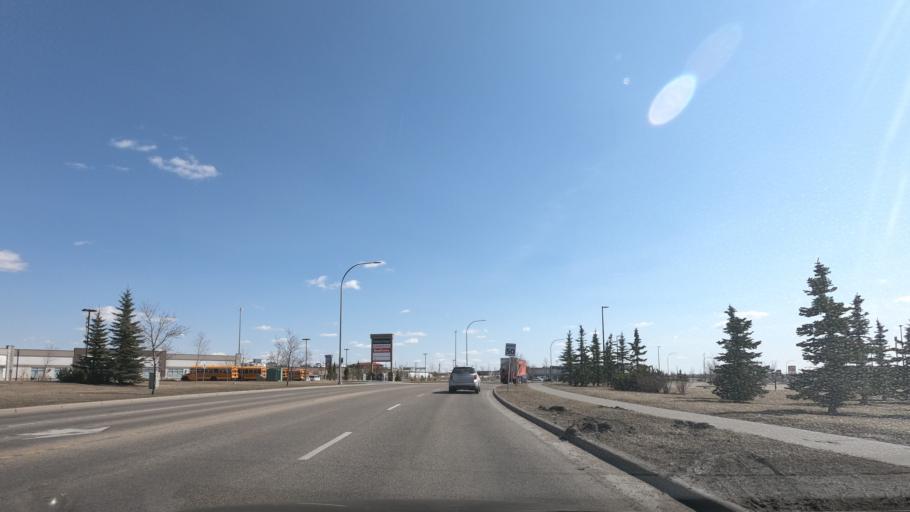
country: CA
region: Alberta
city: Airdrie
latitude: 51.2639
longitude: -114.0048
